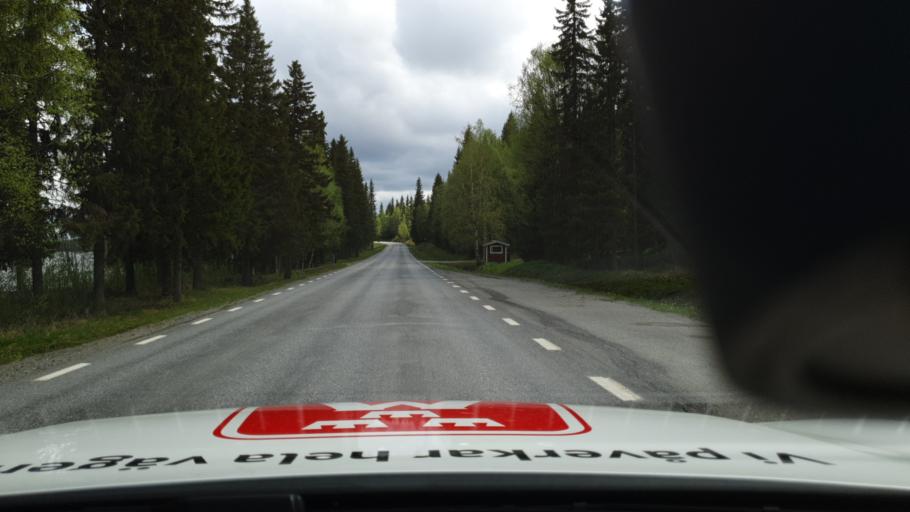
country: SE
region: Vaesterbotten
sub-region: Vilhelmina Kommun
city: Sjoberg
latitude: 64.6611
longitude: 16.3115
